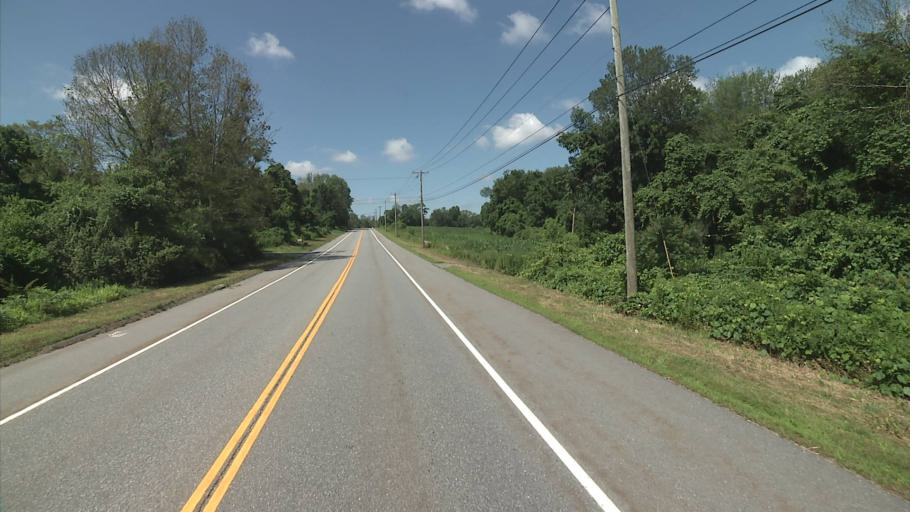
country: US
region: Connecticut
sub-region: Windham County
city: Moosup
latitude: 41.6797
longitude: -71.8750
